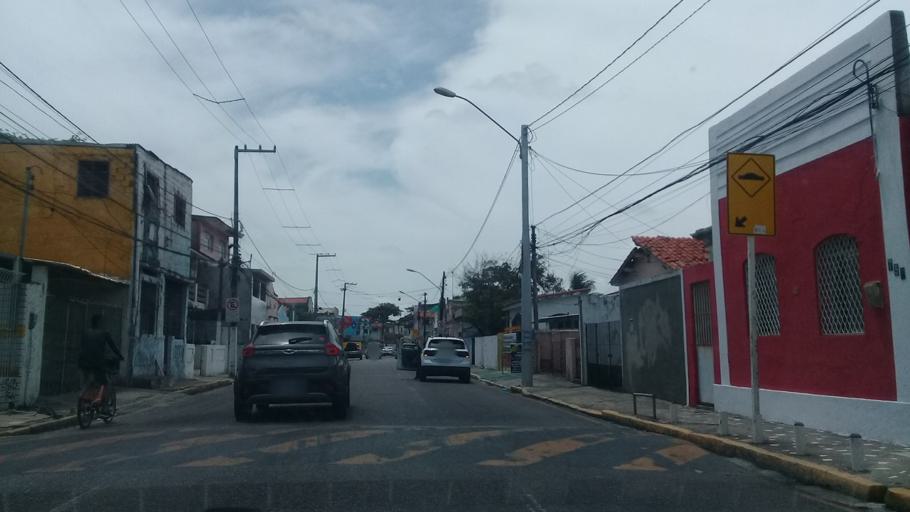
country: BR
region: Pernambuco
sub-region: Olinda
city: Olinda
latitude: -8.0118
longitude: -34.8433
